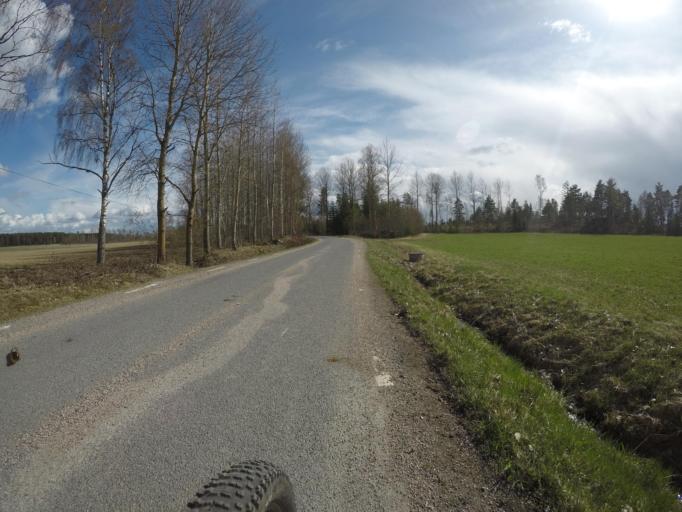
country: SE
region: Vaestmanland
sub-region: Kungsors Kommun
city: Kungsoer
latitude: 59.3086
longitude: 16.1243
